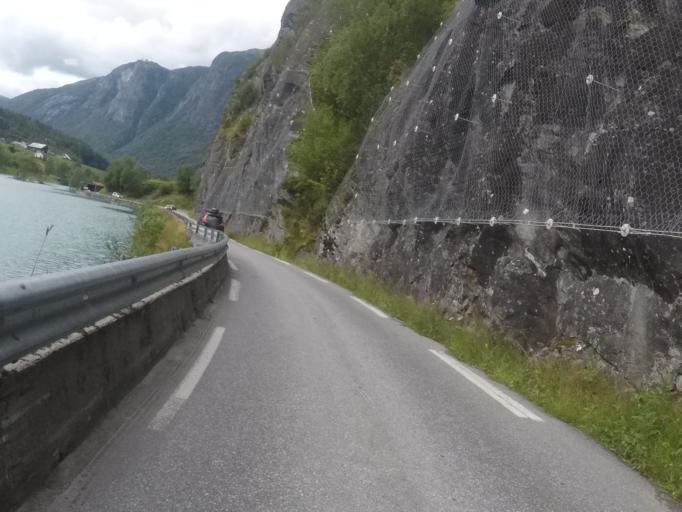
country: NO
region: Sogn og Fjordane
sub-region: Stryn
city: Stryn
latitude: 61.8579
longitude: 6.8947
